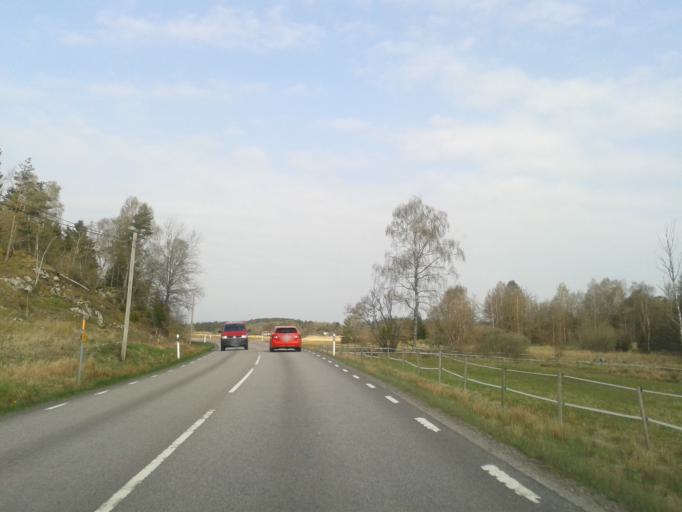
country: SE
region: Vaestra Goetaland
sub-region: Kungalvs Kommun
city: Kode
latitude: 57.8902
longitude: 11.8841
